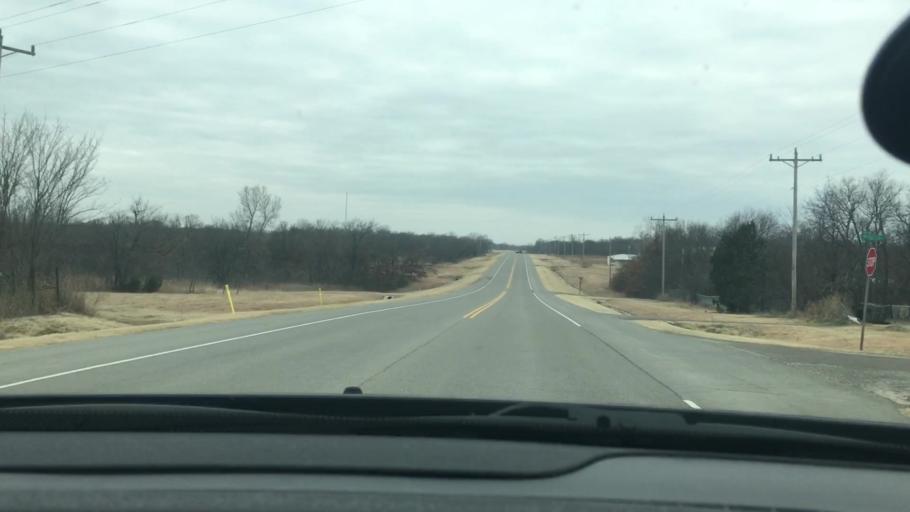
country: US
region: Oklahoma
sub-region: Carter County
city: Healdton
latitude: 34.4815
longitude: -97.4616
